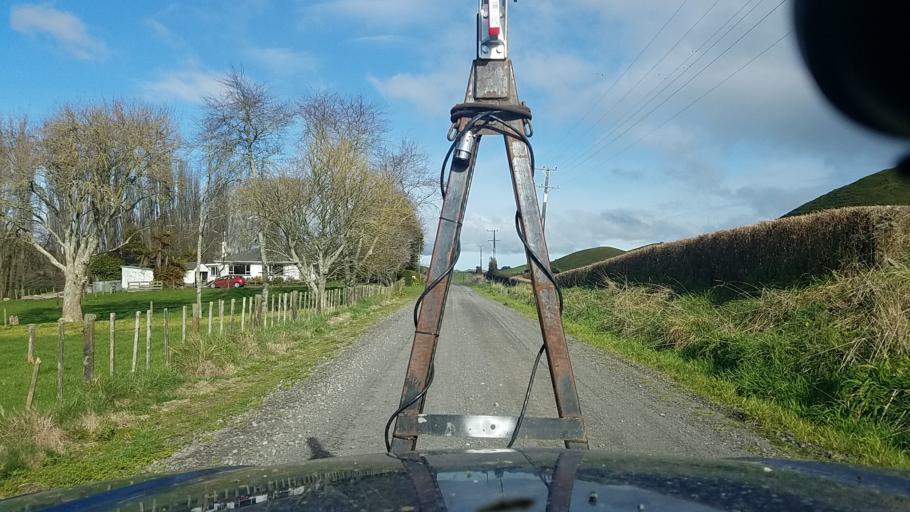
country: NZ
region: Taranaki
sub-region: South Taranaki District
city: Eltham
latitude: -39.3401
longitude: 174.4247
